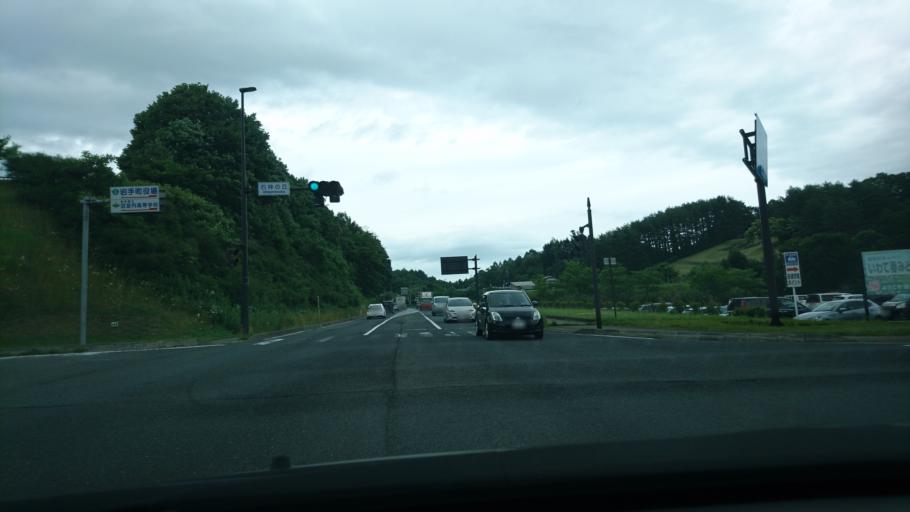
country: JP
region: Iwate
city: Ichinohe
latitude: 39.9694
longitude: 141.2131
